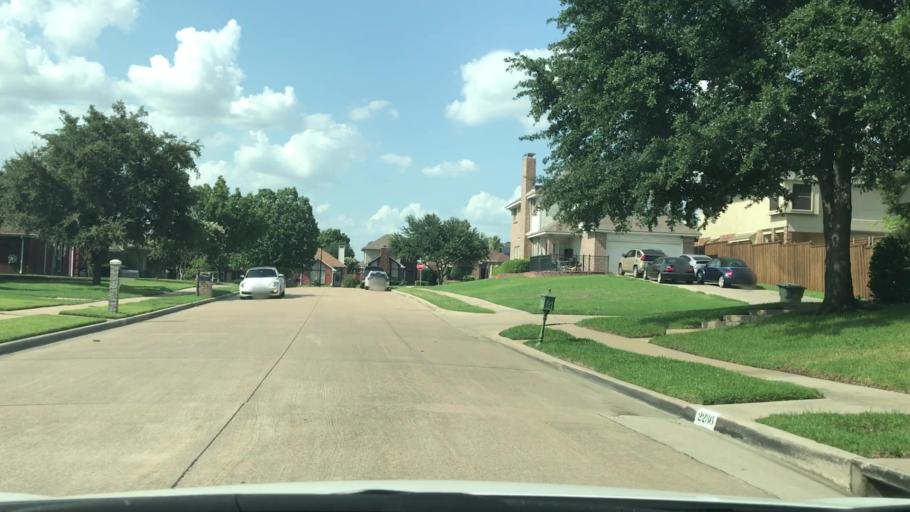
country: US
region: Texas
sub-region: Dallas County
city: Addison
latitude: 32.9724
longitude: -96.8605
